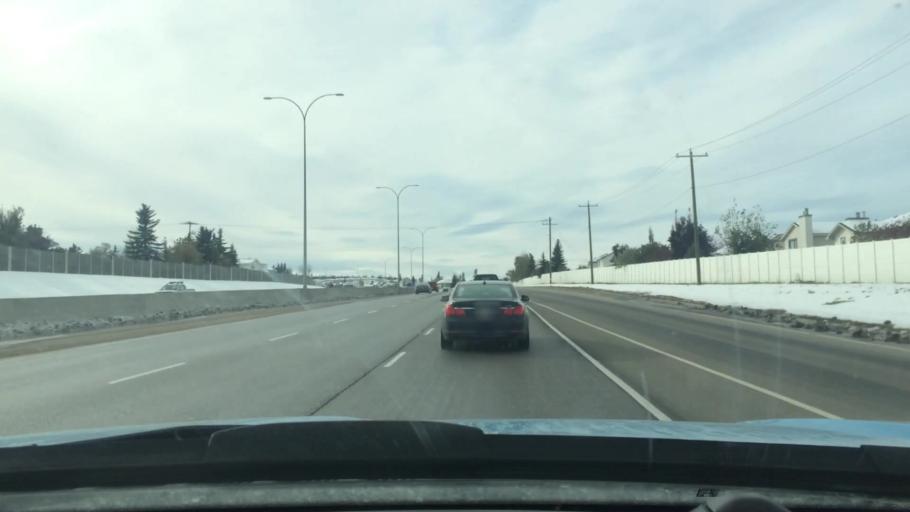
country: CA
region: Alberta
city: Calgary
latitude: 51.1440
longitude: -114.1107
